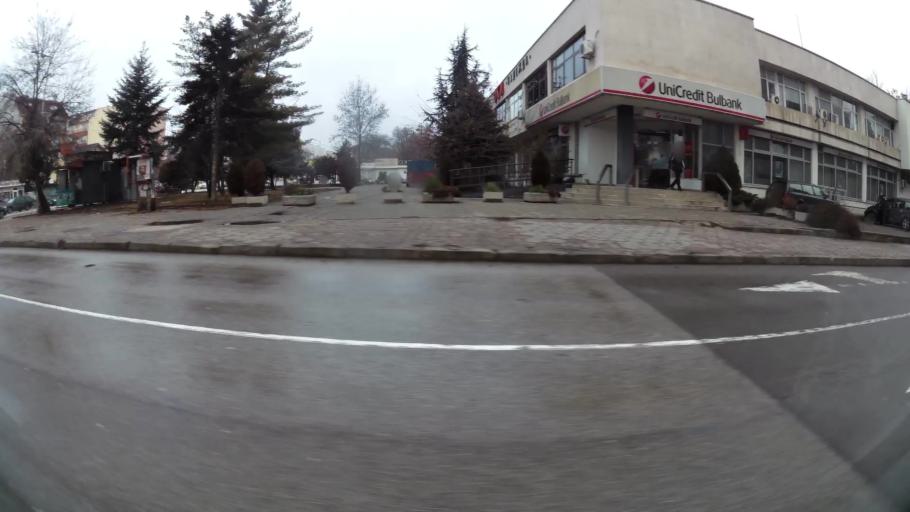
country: BG
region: Sofia-Capital
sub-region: Stolichna Obshtina
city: Sofia
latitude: 42.7241
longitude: 23.3057
